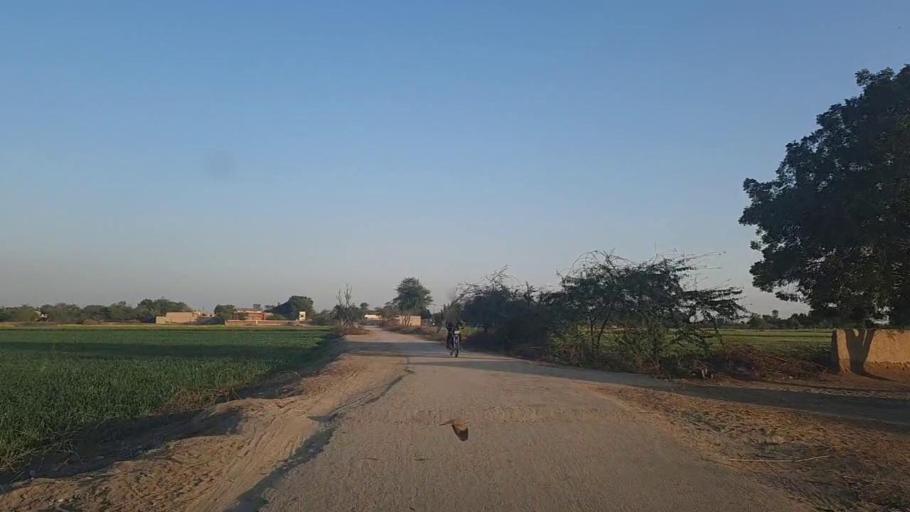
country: PK
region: Sindh
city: Jam Sahib
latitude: 26.3226
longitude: 68.6998
